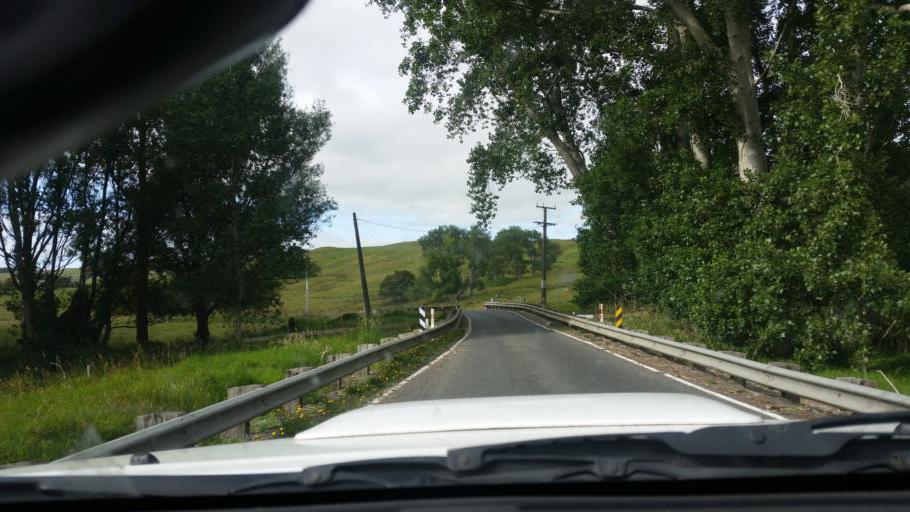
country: NZ
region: Northland
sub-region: Kaipara District
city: Dargaville
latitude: -35.8411
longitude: 173.8435
